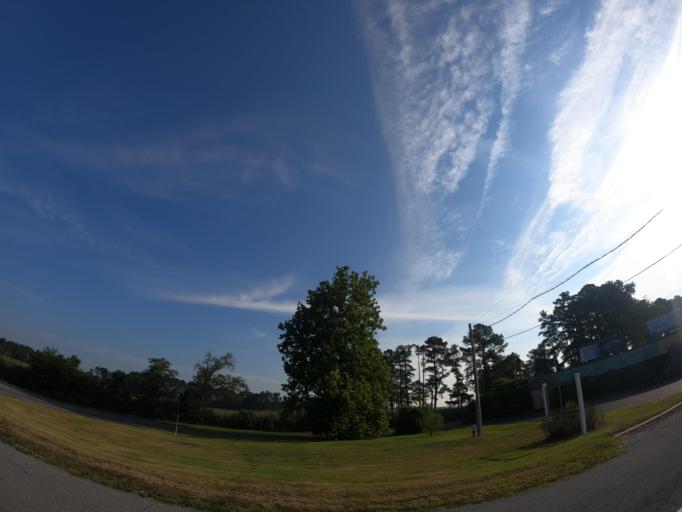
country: US
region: Delaware
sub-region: Sussex County
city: Long Neck
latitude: 38.5570
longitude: -75.1997
